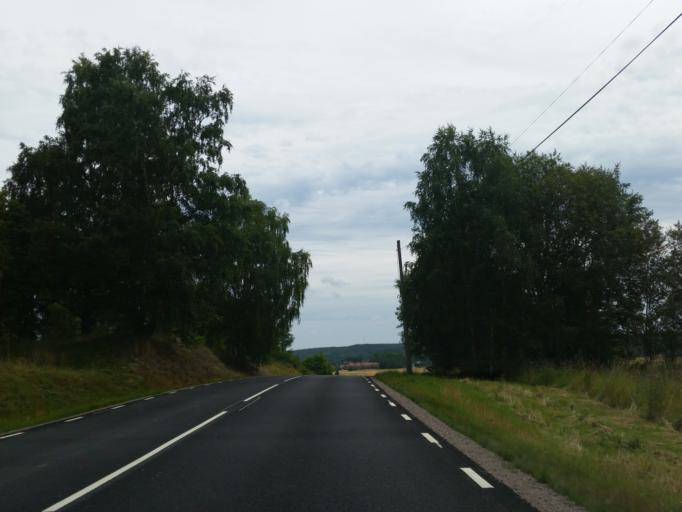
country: SE
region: Soedermanland
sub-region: Strangnas Kommun
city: Mariefred
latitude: 59.2619
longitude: 17.1661
